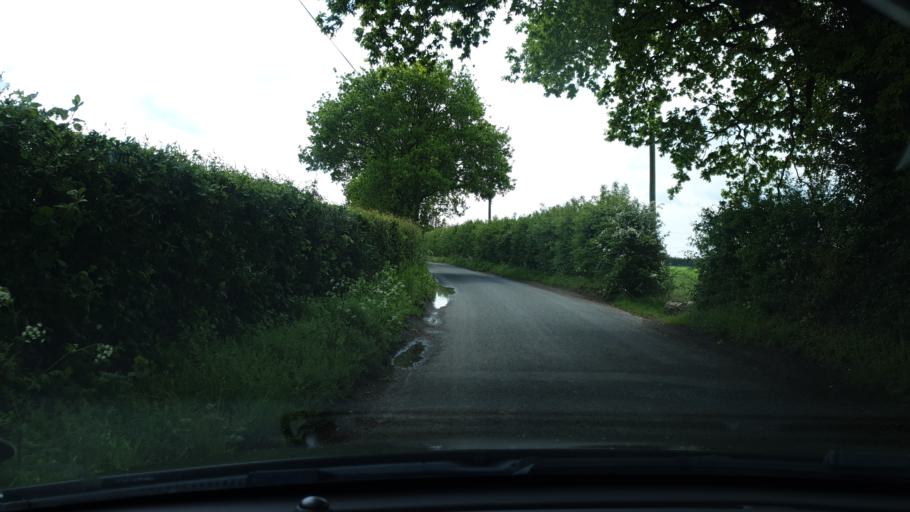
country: GB
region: England
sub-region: Essex
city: Great Bentley
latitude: 51.8745
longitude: 1.0610
